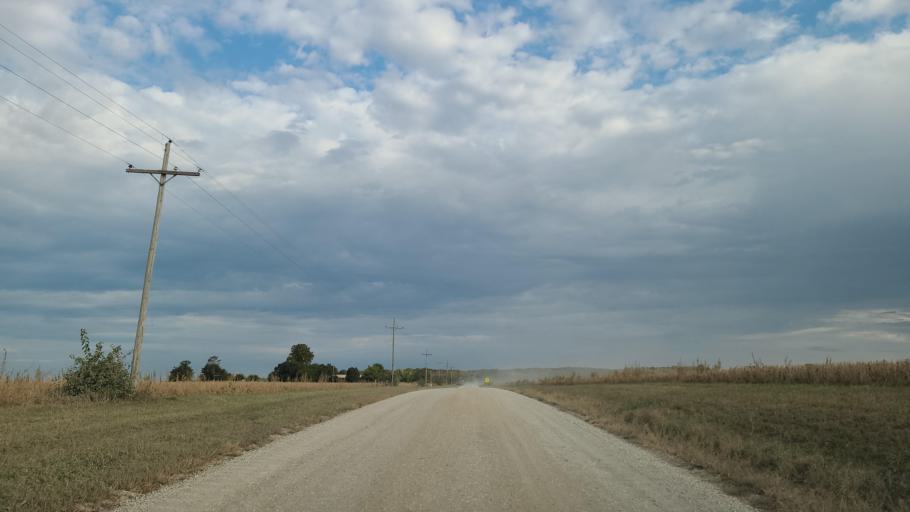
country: US
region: Kansas
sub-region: Douglas County
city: Lawrence
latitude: 39.0050
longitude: -95.2055
